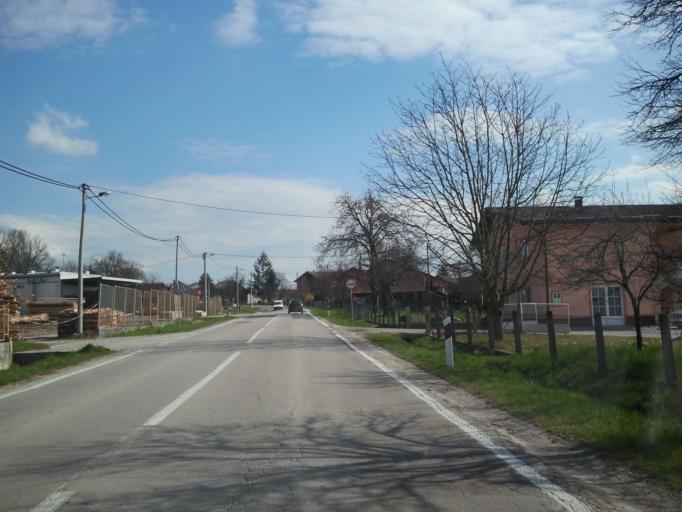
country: HR
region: Karlovacka
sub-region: Grad Karlovac
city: Karlovac
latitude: 45.5681
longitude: 15.5903
